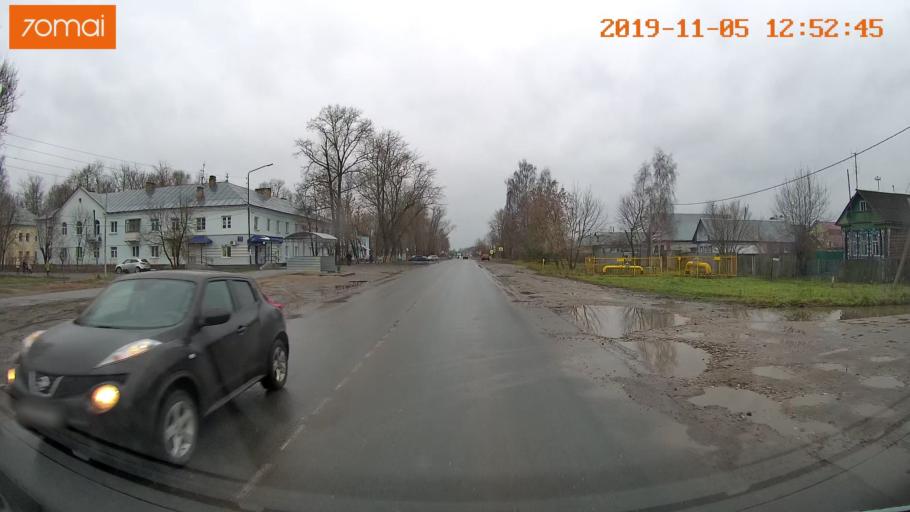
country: RU
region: Ivanovo
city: Kokhma
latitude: 56.9394
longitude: 41.1057
